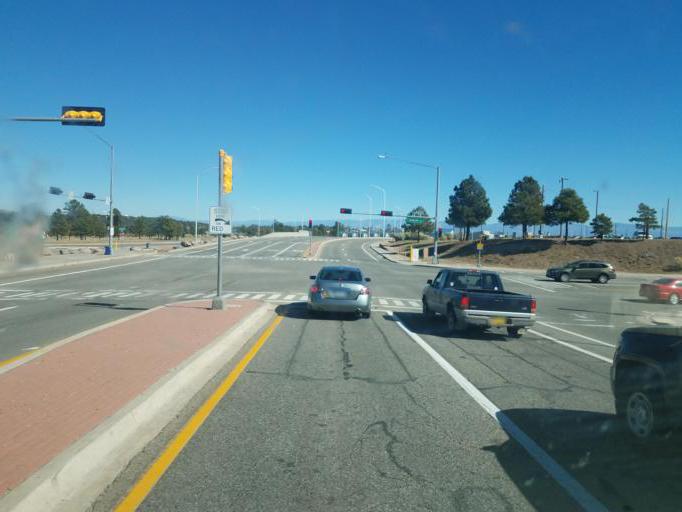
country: US
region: New Mexico
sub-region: Los Alamos County
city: Los Alamos
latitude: 35.8773
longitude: -106.3227
